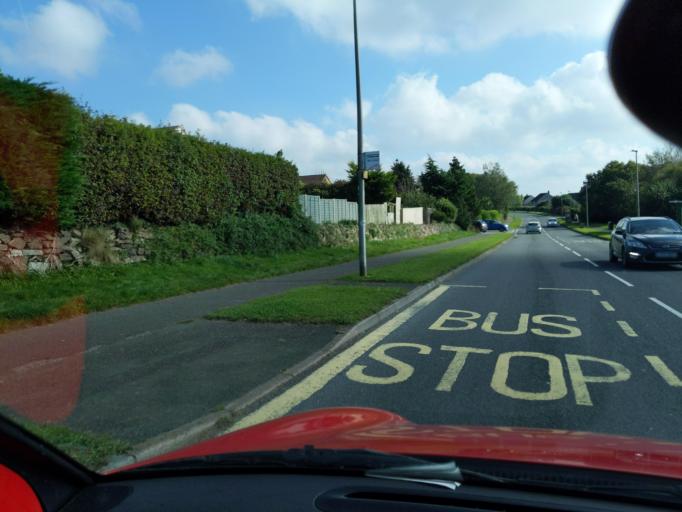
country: GB
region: England
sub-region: Devon
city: Yelverton
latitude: 50.4344
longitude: -4.1057
